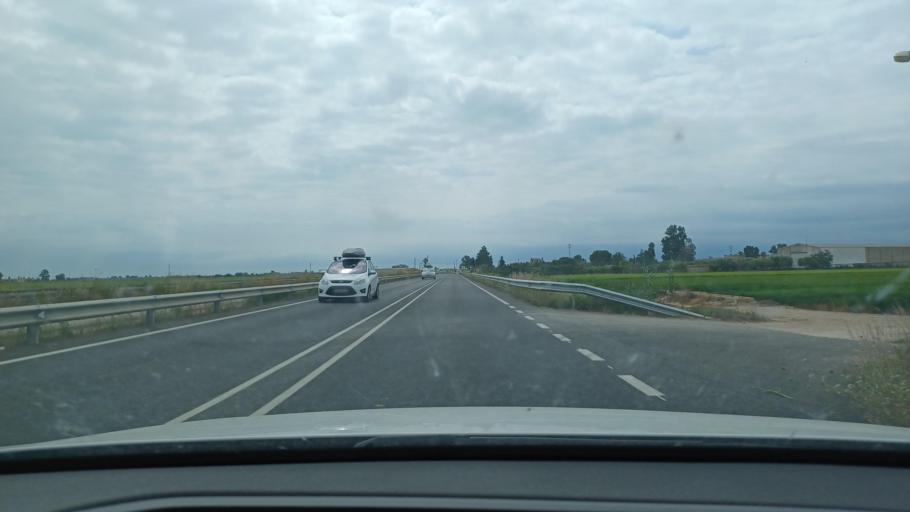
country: ES
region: Catalonia
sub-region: Provincia de Tarragona
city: Deltebre
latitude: 40.7163
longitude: 0.7522
